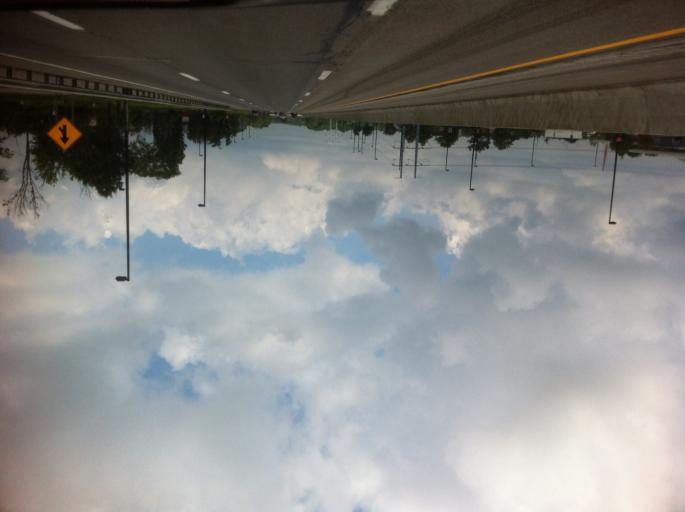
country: US
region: Ohio
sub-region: Cuyahoga County
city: Broadview Heights
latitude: 41.2919
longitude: -81.6729
